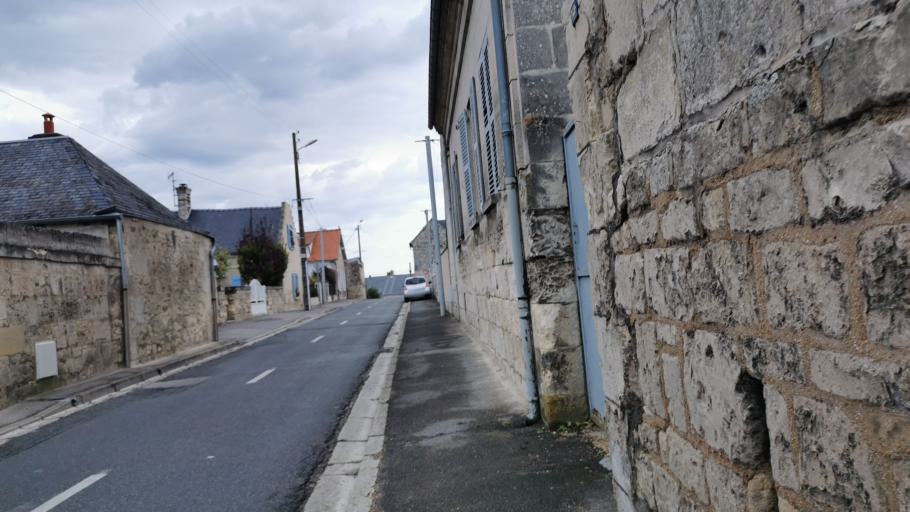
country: FR
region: Picardie
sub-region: Departement de l'Aisne
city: Billy-sur-Aisne
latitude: 49.3550
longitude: 3.3835
